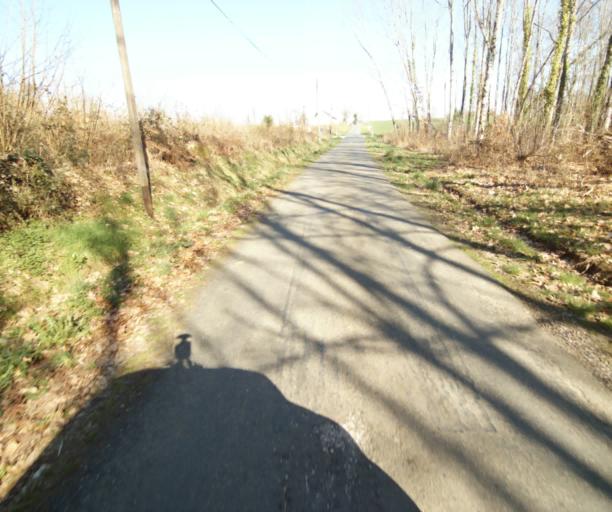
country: FR
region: Limousin
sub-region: Departement de la Correze
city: Seilhac
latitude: 45.3863
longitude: 1.7577
